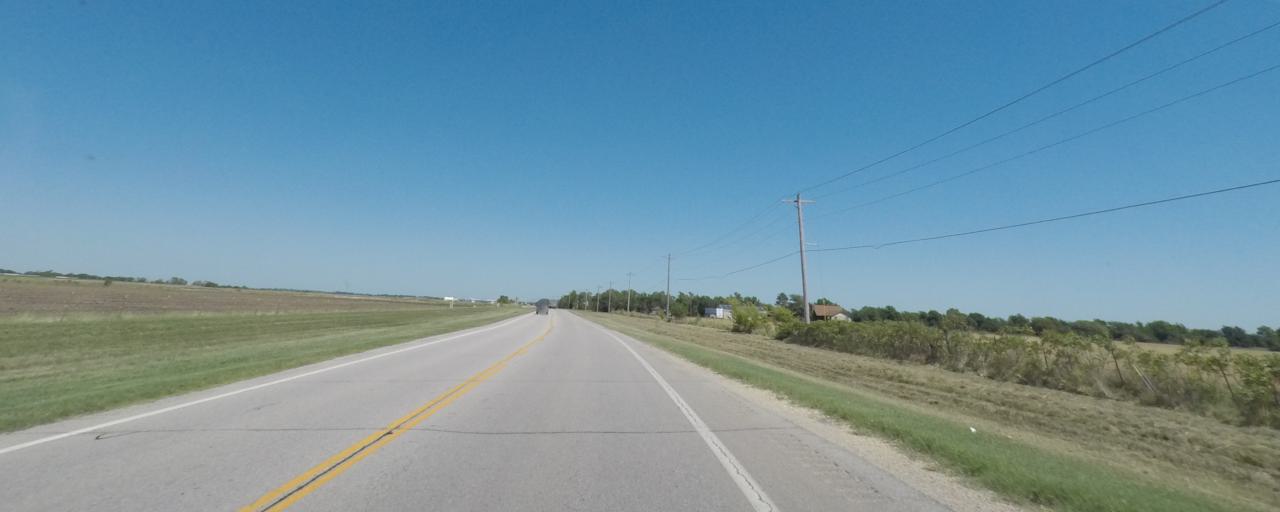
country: US
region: Kansas
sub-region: Sumner County
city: Wellington
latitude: 37.3086
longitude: -97.3849
